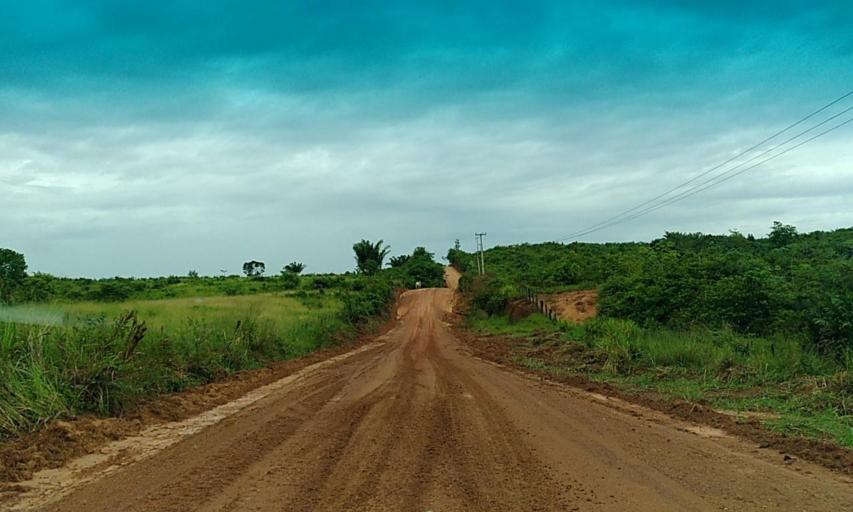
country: BR
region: Para
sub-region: Altamira
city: Altamira
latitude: -3.0852
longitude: -51.6346
